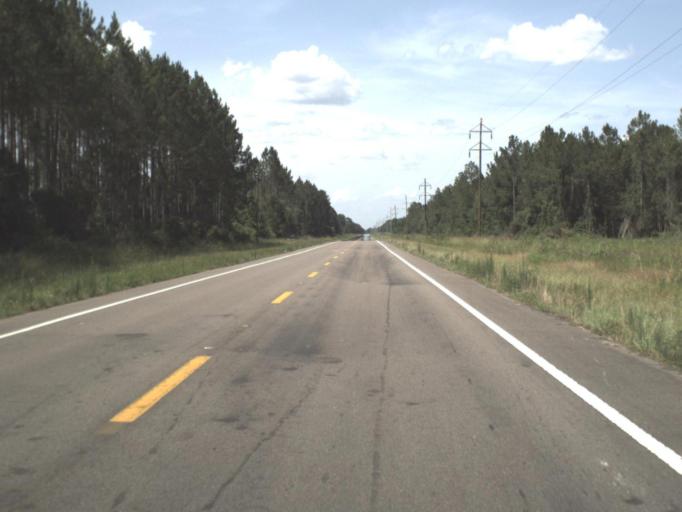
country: US
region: Florida
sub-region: Gilchrist County
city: Trenton
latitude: 29.7005
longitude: -82.7588
